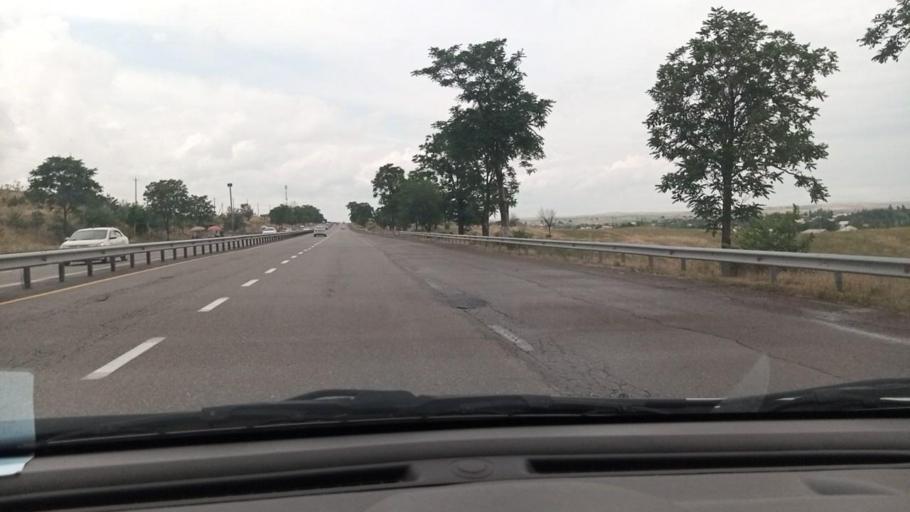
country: UZ
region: Toshkent
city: Ohangaron
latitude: 40.9773
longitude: 69.5430
